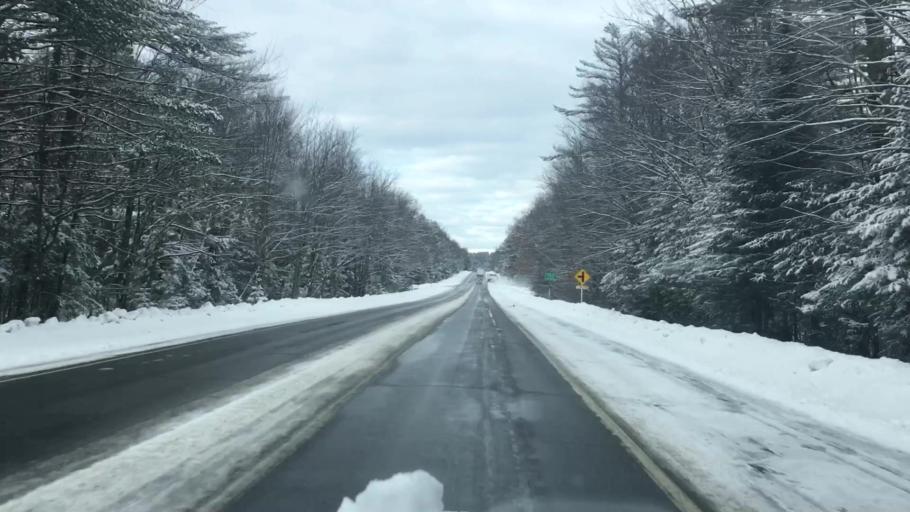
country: US
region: Maine
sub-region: Cumberland County
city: Bridgton
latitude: 44.0000
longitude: -70.6624
